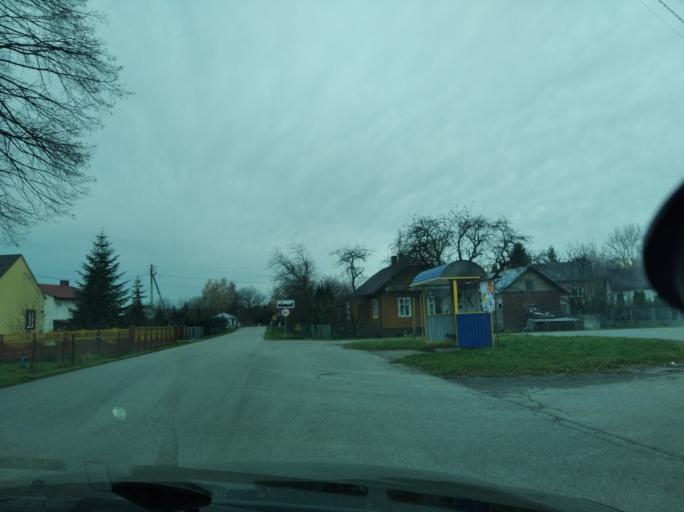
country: PL
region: Subcarpathian Voivodeship
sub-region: Powiat przeworski
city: Grzeska
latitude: 50.0931
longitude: 22.4195
